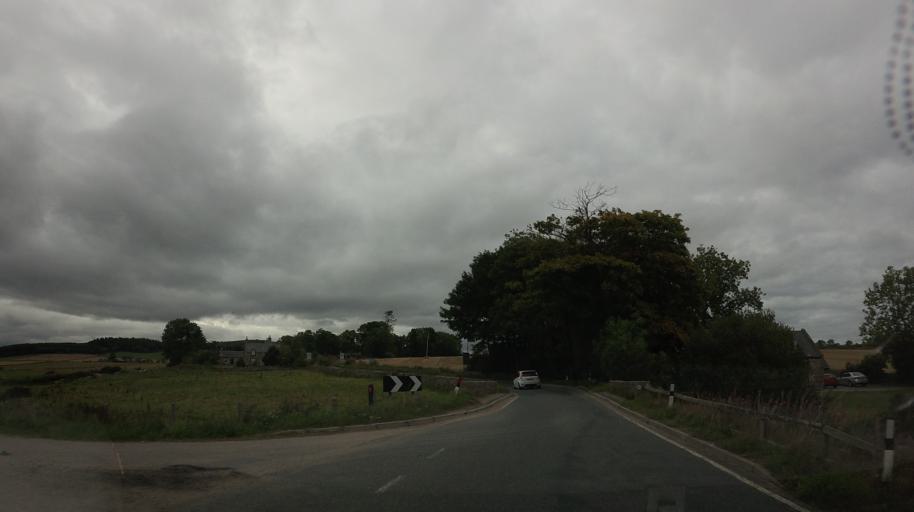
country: GB
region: Scotland
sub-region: Aberdeenshire
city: Kemnay
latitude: 57.1357
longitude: -2.4301
